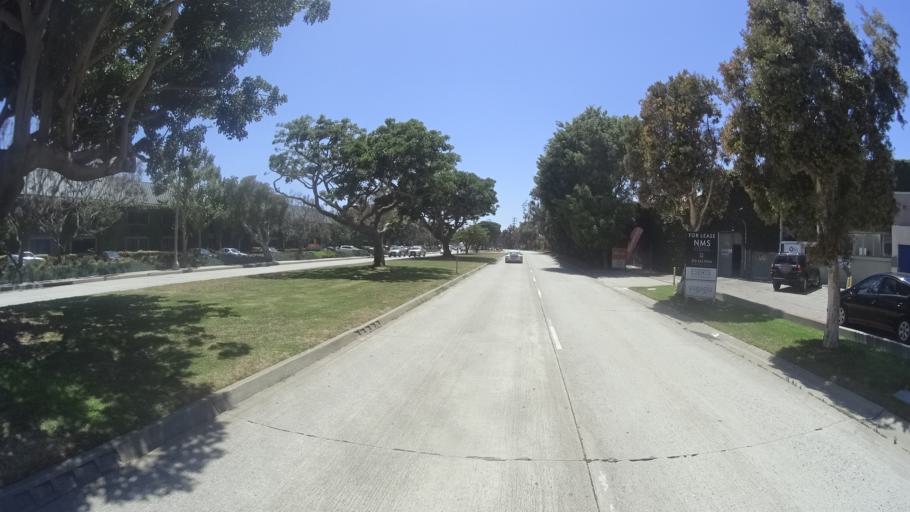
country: US
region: California
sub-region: Los Angeles County
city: Santa Monica
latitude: 34.0308
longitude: -118.4622
